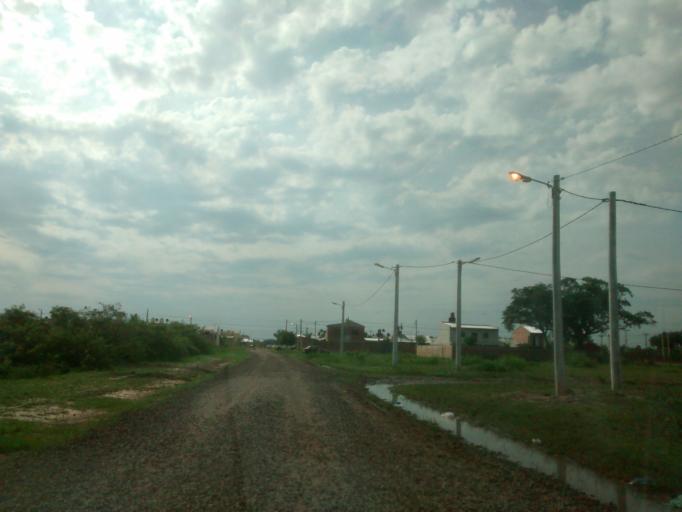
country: AR
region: Chaco
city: Fontana
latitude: -27.4023
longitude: -58.9828
